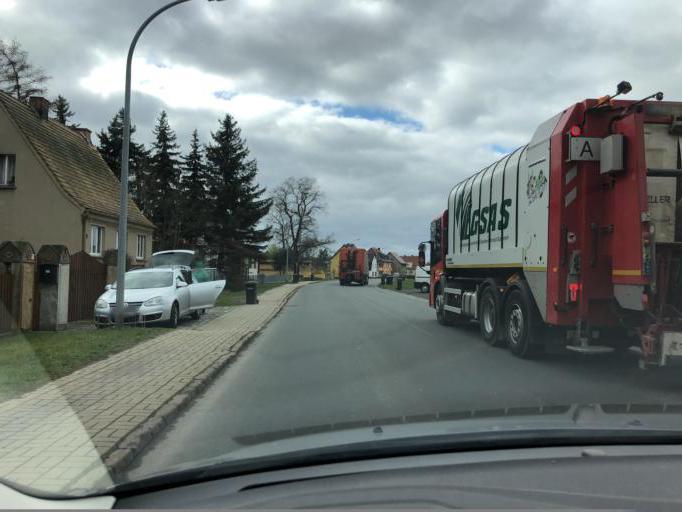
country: DE
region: Saxony-Anhalt
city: Zeitz
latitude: 51.0717
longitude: 12.1523
